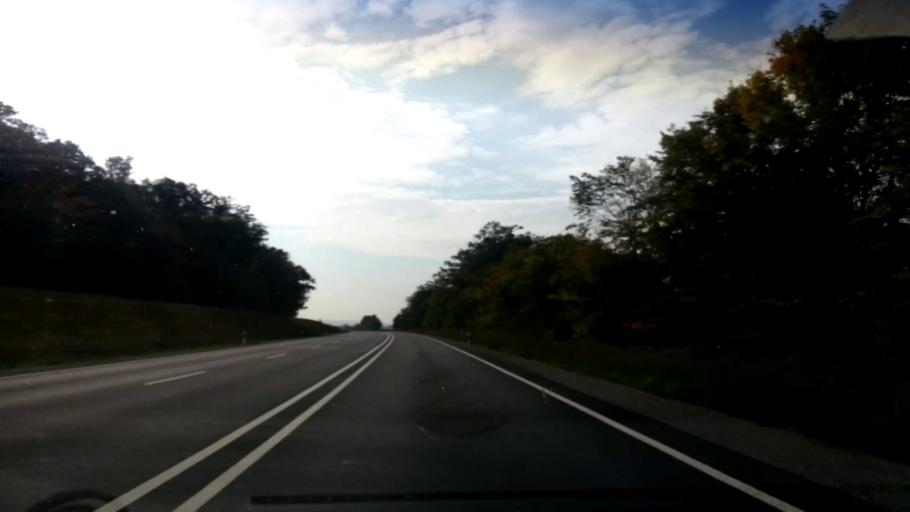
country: DE
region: Bavaria
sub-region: Regierungsbezirk Unterfranken
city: Gerolzhofen
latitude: 49.8821
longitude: 10.3568
